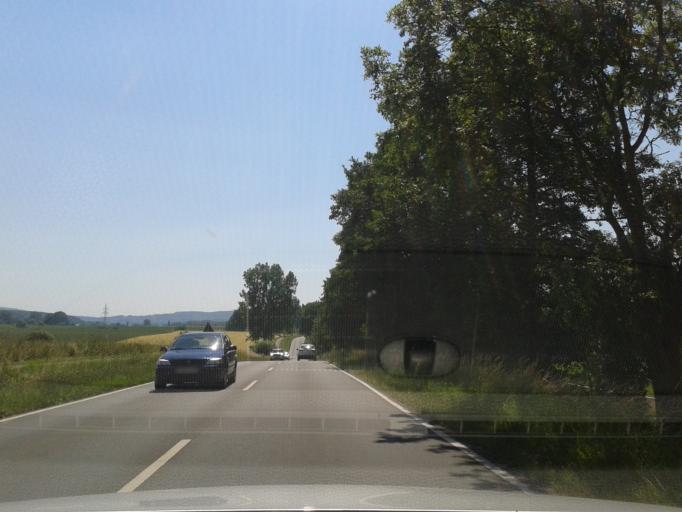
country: DE
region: North Rhine-Westphalia
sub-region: Regierungsbezirk Detmold
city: Dorentrup
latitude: 52.0230
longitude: 9.0597
